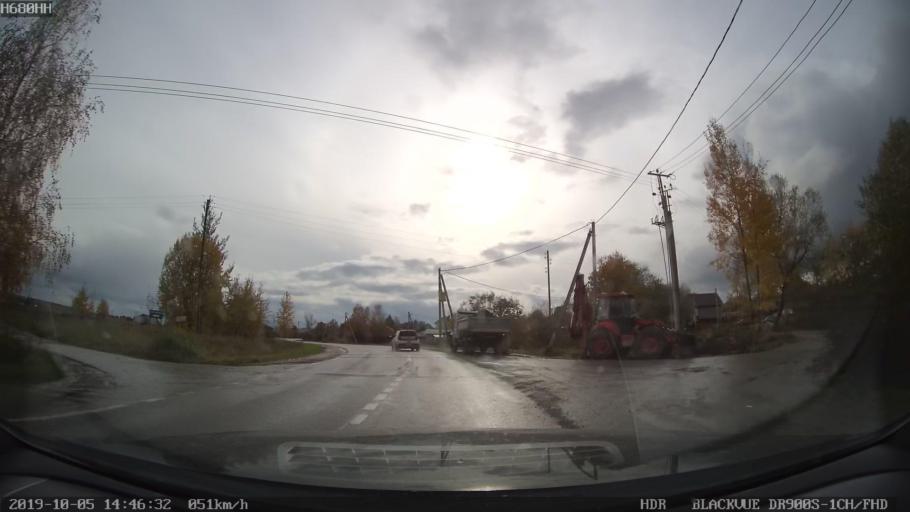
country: RU
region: Moskovskaya
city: Solnechnogorsk
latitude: 56.2258
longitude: 36.9075
